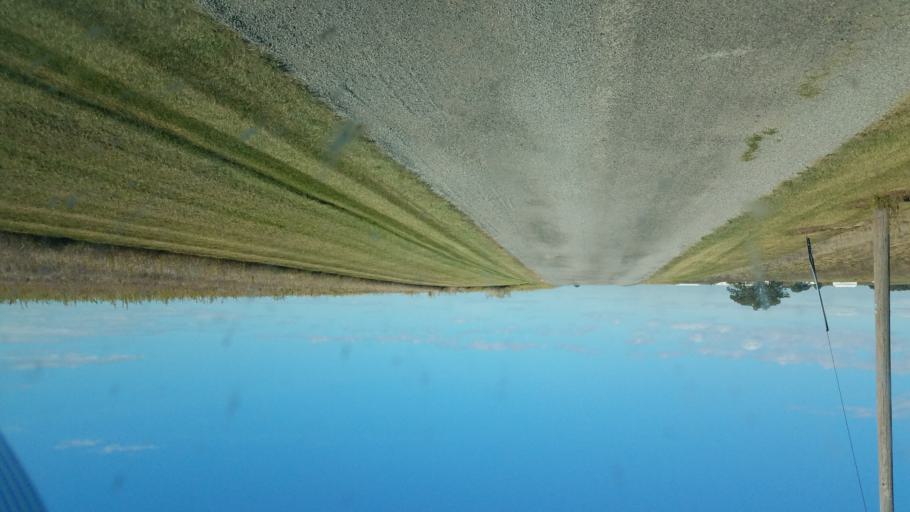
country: US
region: Ohio
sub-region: Wyandot County
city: Upper Sandusky
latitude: 40.7930
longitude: -83.2331
